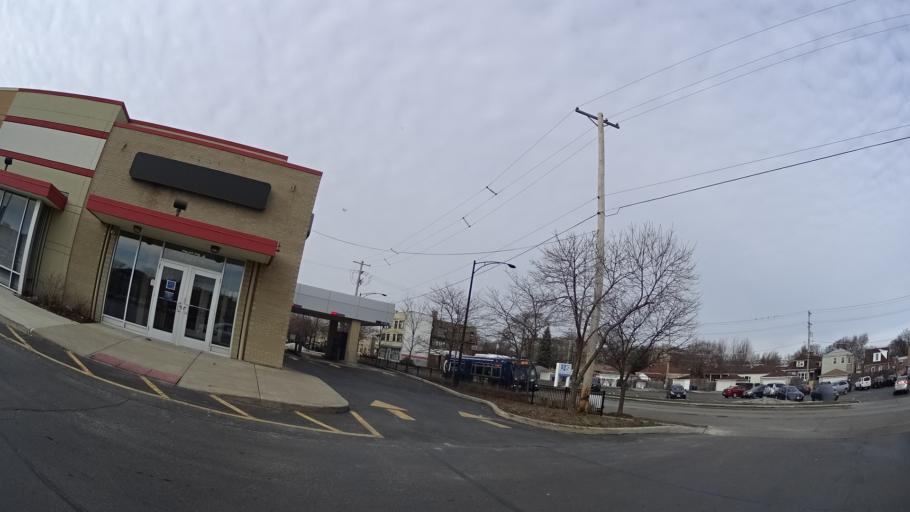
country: US
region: Illinois
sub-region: Cook County
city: Evanston
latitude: 42.0192
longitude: -87.6913
